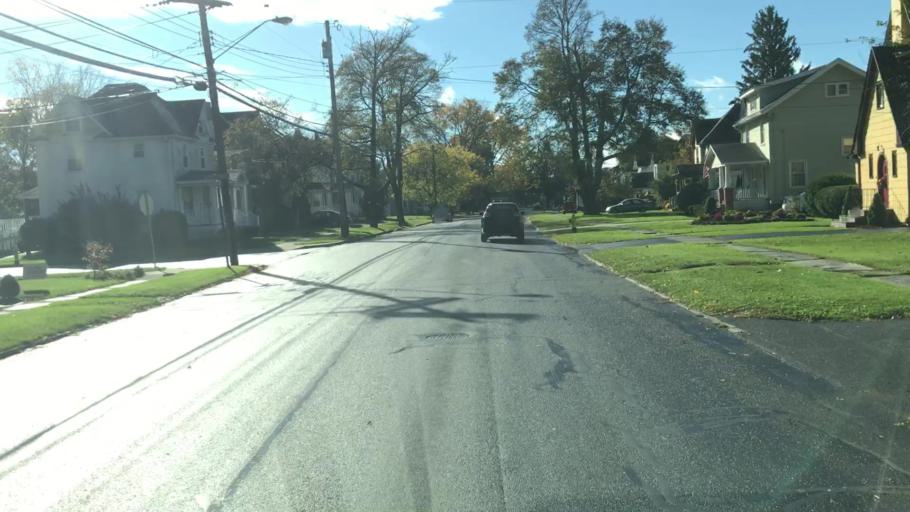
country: US
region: New York
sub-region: Cayuga County
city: Auburn
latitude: 42.9228
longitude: -76.5538
